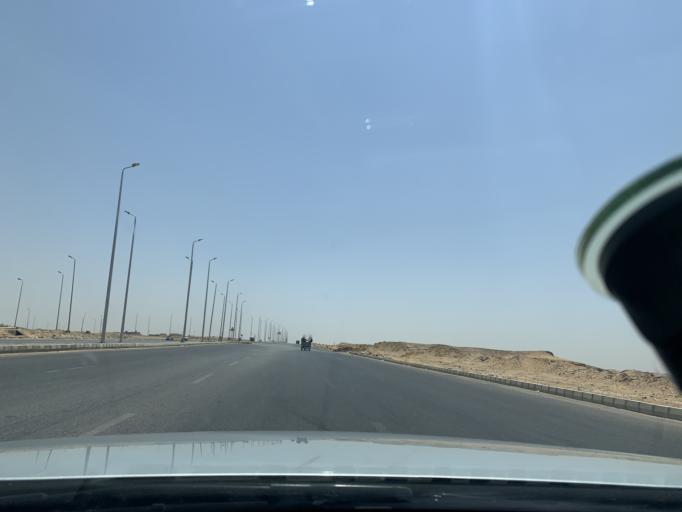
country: EG
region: Muhafazat al Qahirah
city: Halwan
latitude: 29.9936
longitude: 31.4687
